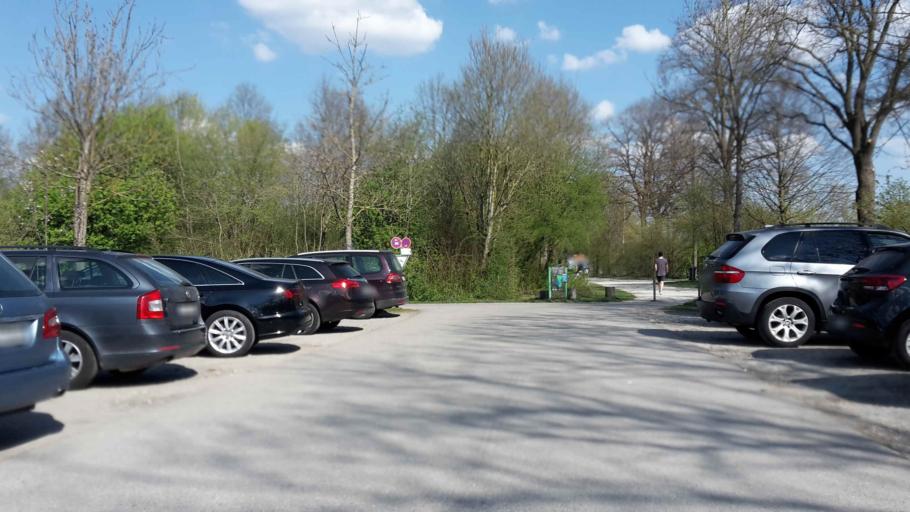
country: DE
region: Bavaria
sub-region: Upper Bavaria
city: Grobenzell
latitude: 48.2003
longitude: 11.4140
